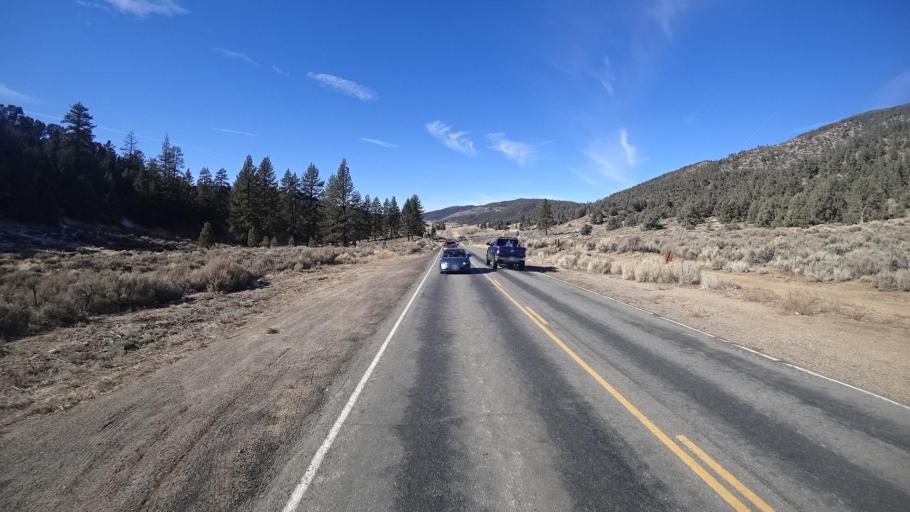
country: US
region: California
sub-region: Kern County
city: Frazier Park
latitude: 34.8270
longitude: -119.0186
